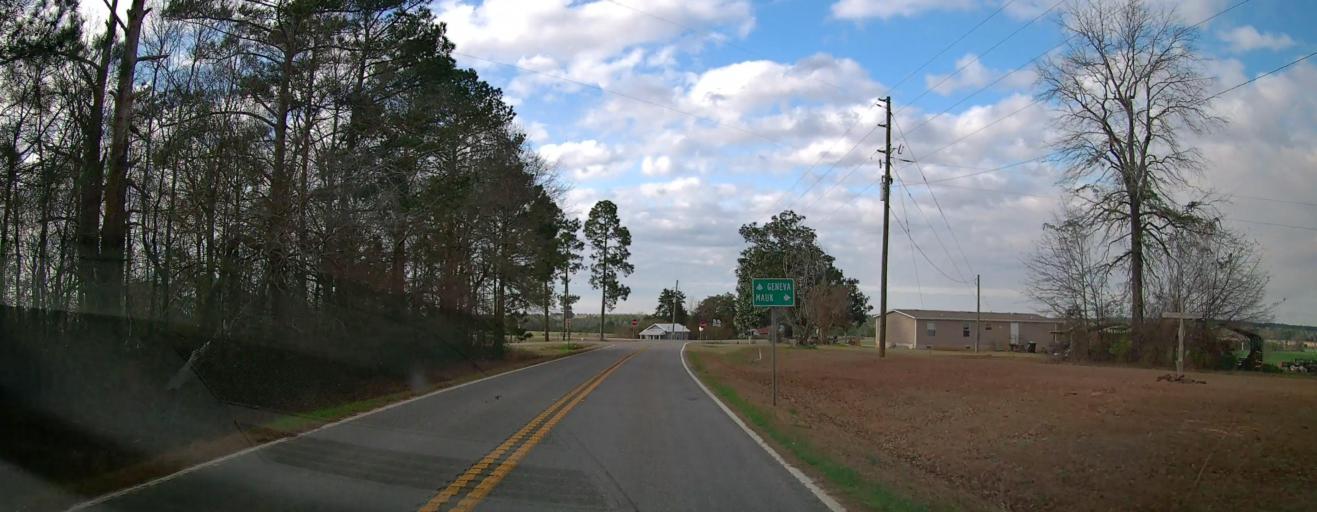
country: US
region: Georgia
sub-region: Marion County
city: Buena Vista
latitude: 32.4523
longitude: -84.4441
